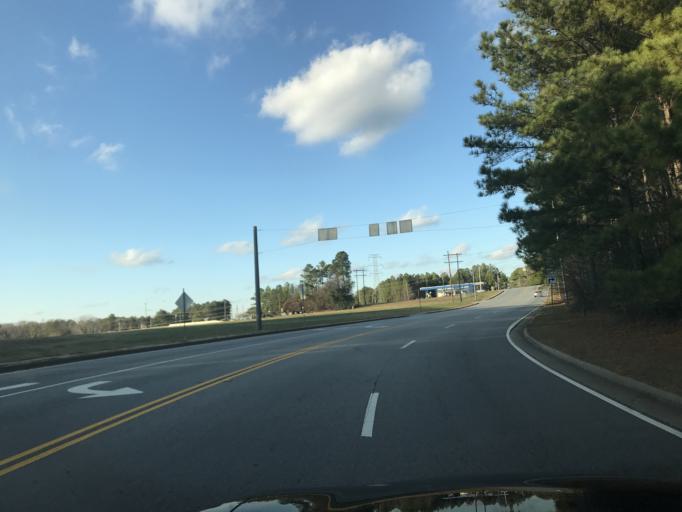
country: US
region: Georgia
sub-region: Fulton County
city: College Park
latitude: 33.6325
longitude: -84.4683
